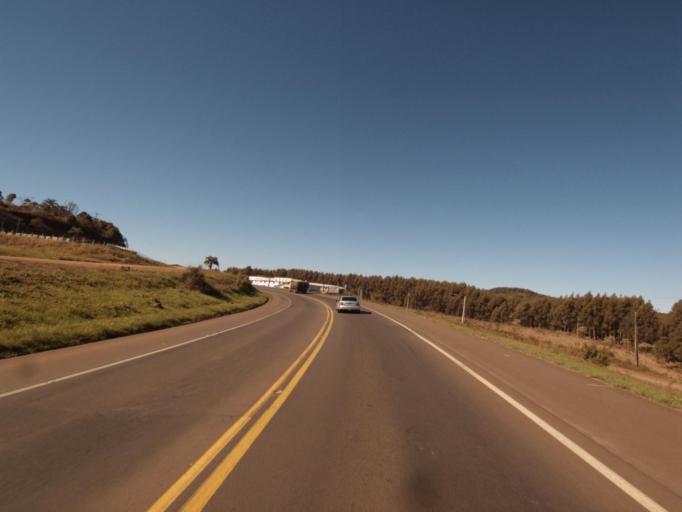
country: BR
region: Santa Catarina
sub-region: Chapeco
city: Chapeco
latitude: -26.9969
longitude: -52.6147
